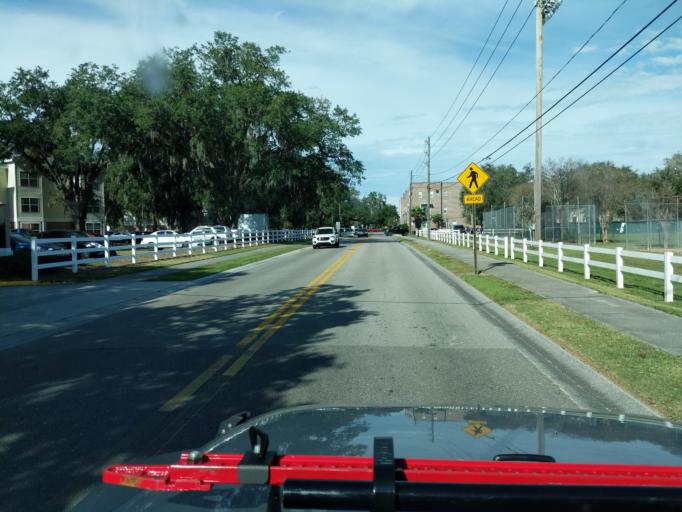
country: US
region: Florida
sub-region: Orange County
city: Winter Garden
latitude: 28.5622
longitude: -81.5919
